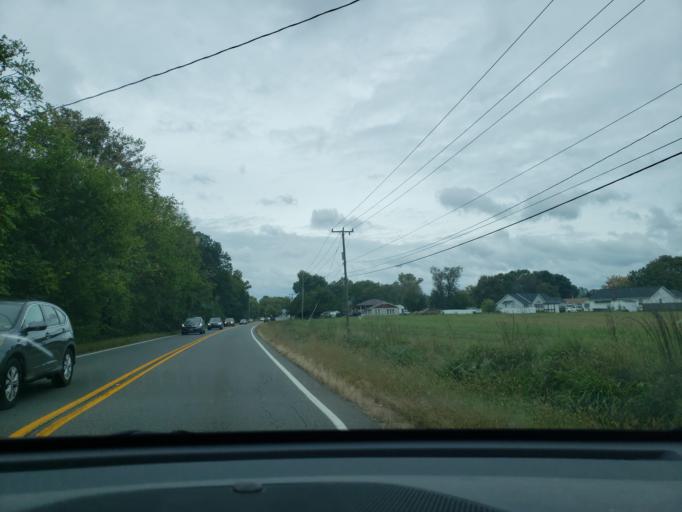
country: US
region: Virginia
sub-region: City of Fredericksburg
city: Fredericksburg
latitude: 38.2443
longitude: -77.4197
